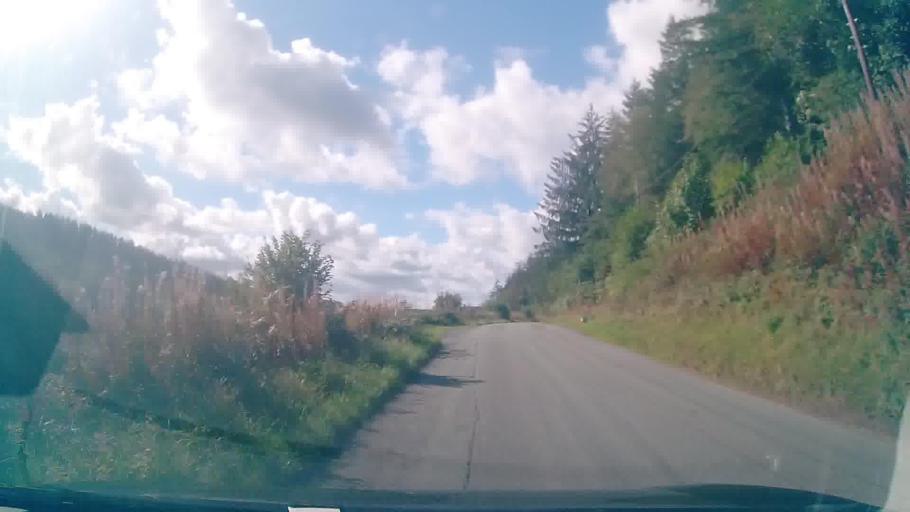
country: GB
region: Wales
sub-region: Sir Powys
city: Llangynog
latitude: 52.7671
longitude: -3.4229
